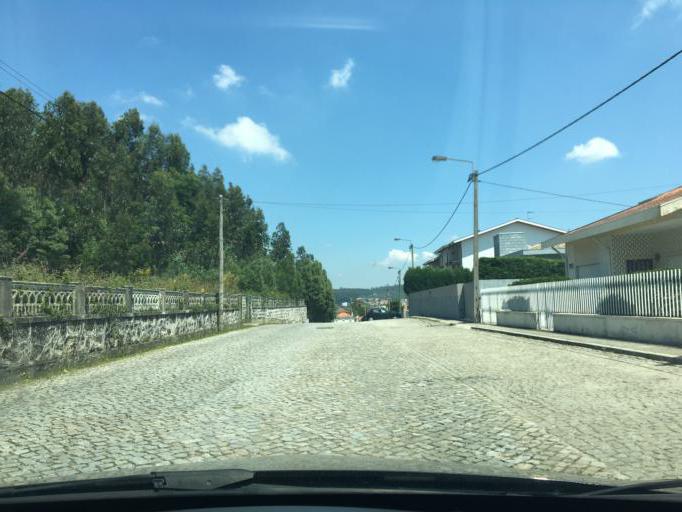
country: PT
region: Porto
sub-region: Maia
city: Anta
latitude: 41.2663
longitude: -8.6191
